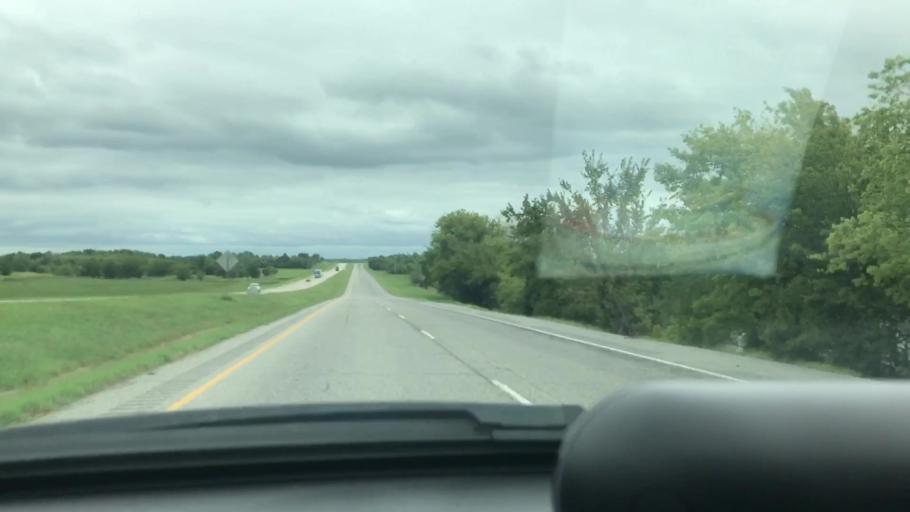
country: US
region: Oklahoma
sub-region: Wagoner County
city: Wagoner
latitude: 35.9813
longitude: -95.3795
